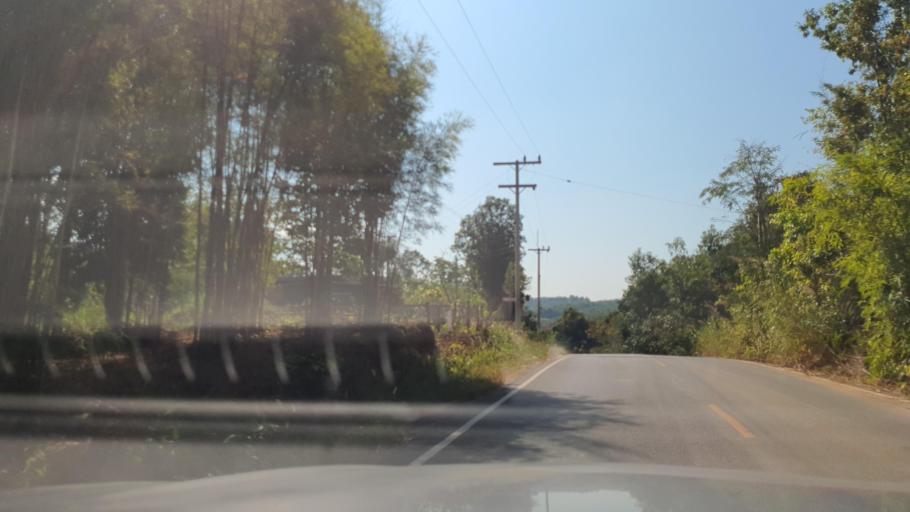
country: TH
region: Nan
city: Pua
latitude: 19.1680
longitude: 100.9092
